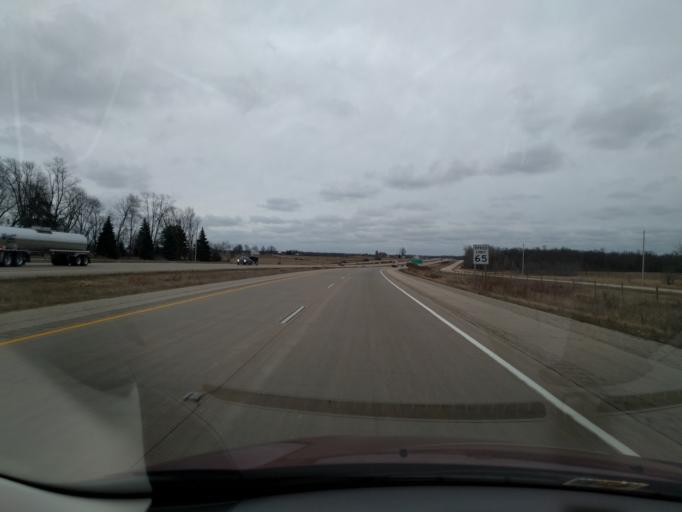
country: US
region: Wisconsin
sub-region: Winnebago County
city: Winneconne
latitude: 44.2325
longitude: -88.7231
